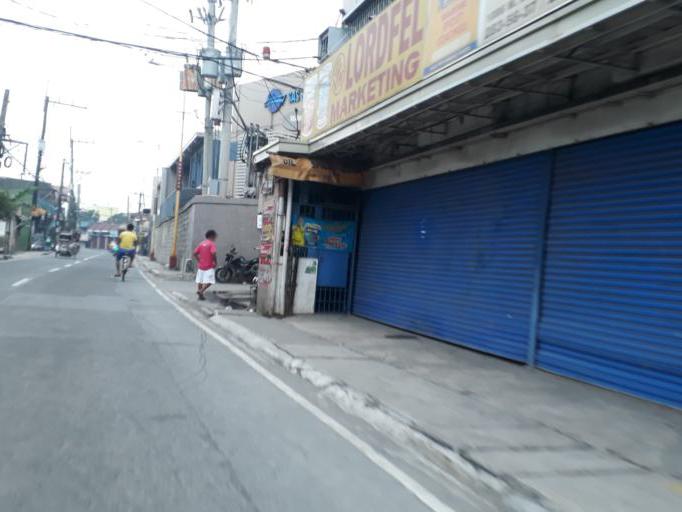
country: PH
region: Calabarzon
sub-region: Province of Rizal
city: Navotas
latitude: 14.6648
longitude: 120.9447
